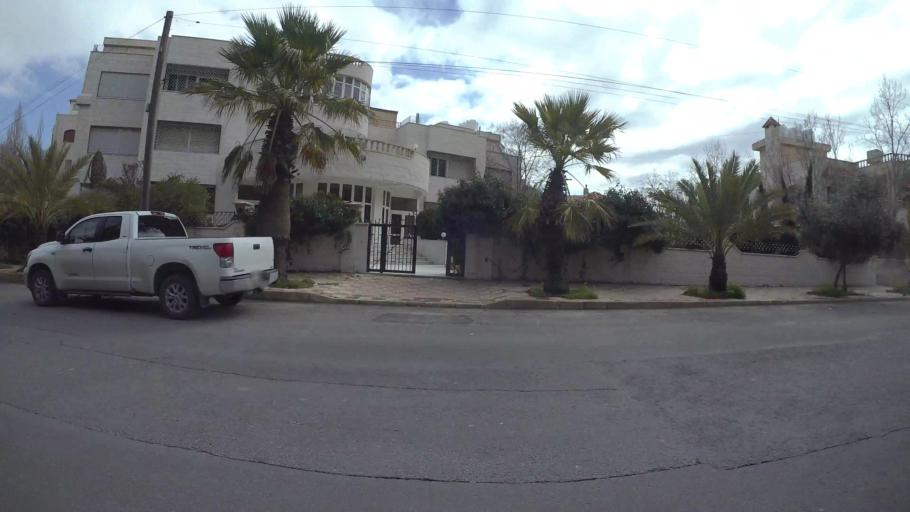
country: JO
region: Amman
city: Al Jubayhah
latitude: 32.0041
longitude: 35.8362
